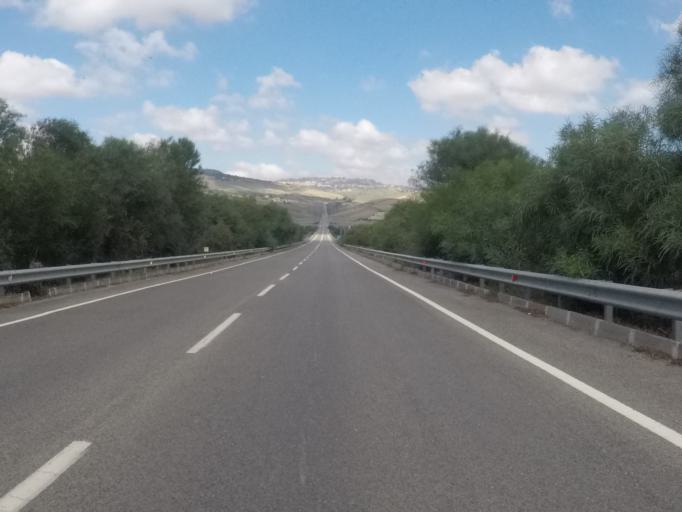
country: IT
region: Sicily
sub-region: Enna
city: Pietraperzia
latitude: 37.4489
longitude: 14.1156
